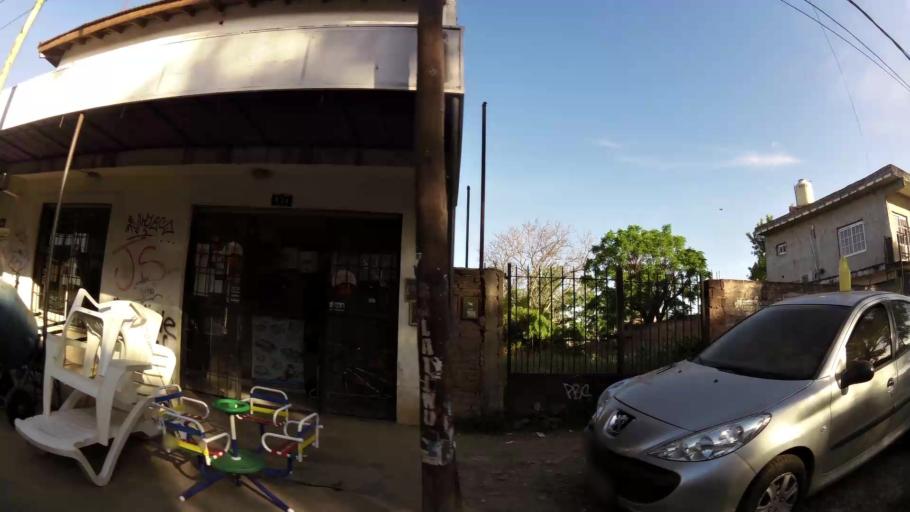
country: AR
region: Buenos Aires
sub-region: Partido de Quilmes
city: Quilmes
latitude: -34.8230
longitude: -58.2107
